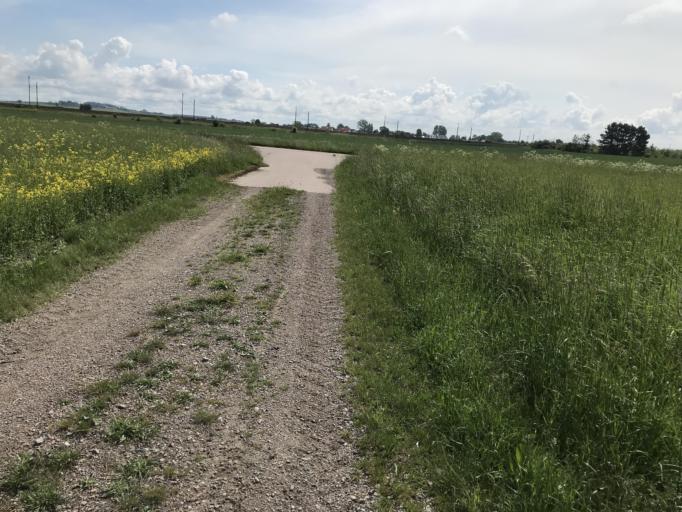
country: SE
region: Skane
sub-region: Landskrona
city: Landskrona
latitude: 55.8988
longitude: 12.8472
